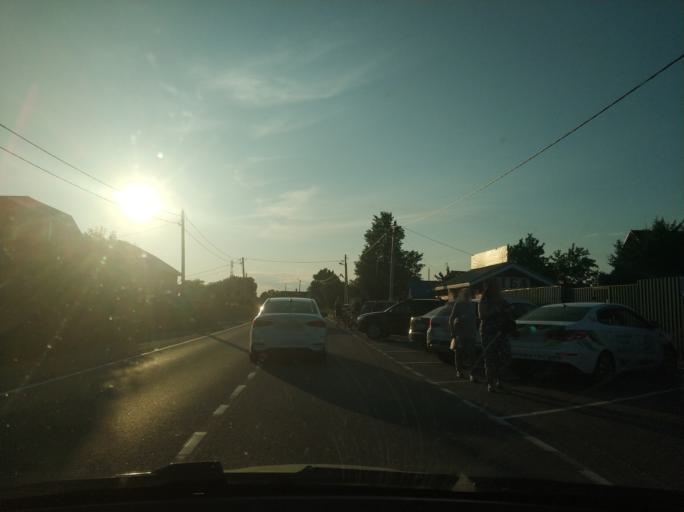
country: RU
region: Leningrad
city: Borisova Griva
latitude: 60.0842
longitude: 31.0296
